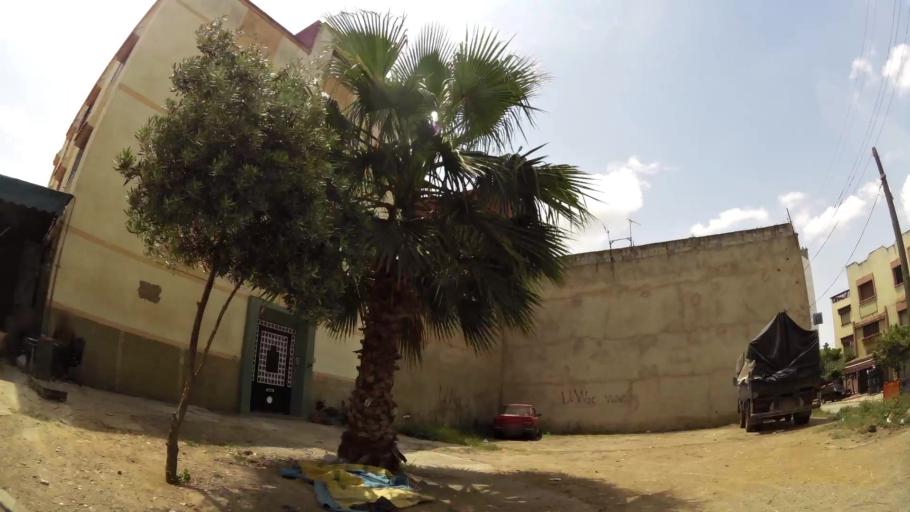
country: MA
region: Rabat-Sale-Zemmour-Zaer
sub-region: Khemisset
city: Tiflet
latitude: 34.0098
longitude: -6.5299
